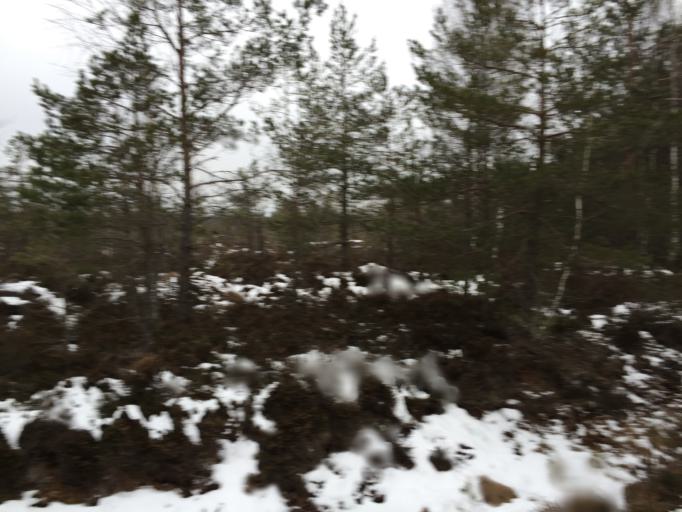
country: LV
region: Saulkrastu
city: Saulkrasti
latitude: 57.2374
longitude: 24.5060
